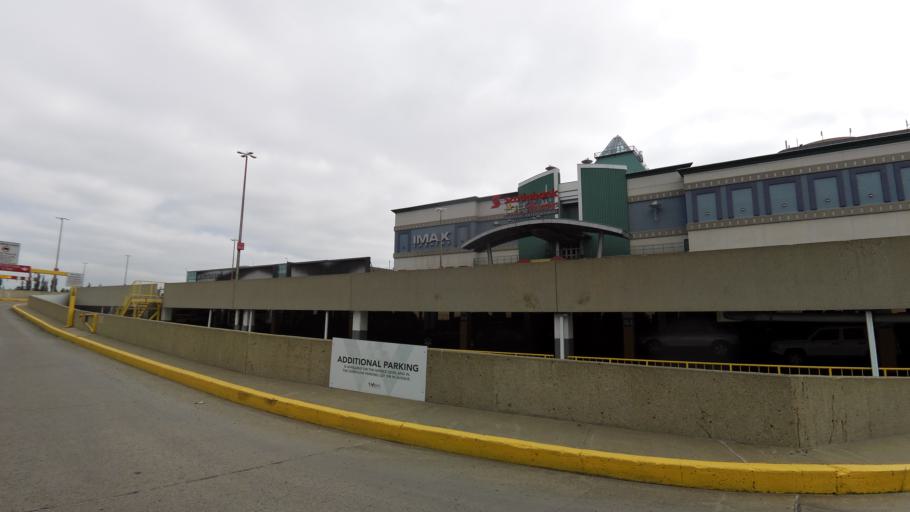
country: CA
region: Alberta
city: St. Albert
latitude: 53.5226
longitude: -113.6299
